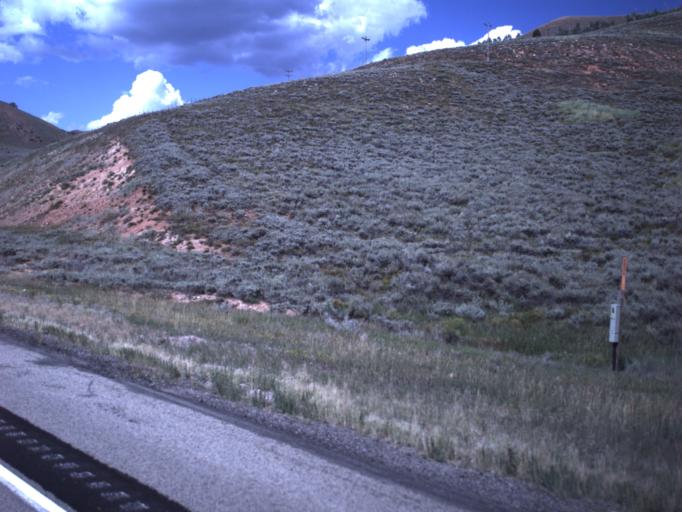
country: US
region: Utah
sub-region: Wasatch County
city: Heber
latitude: 40.2055
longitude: -111.1044
